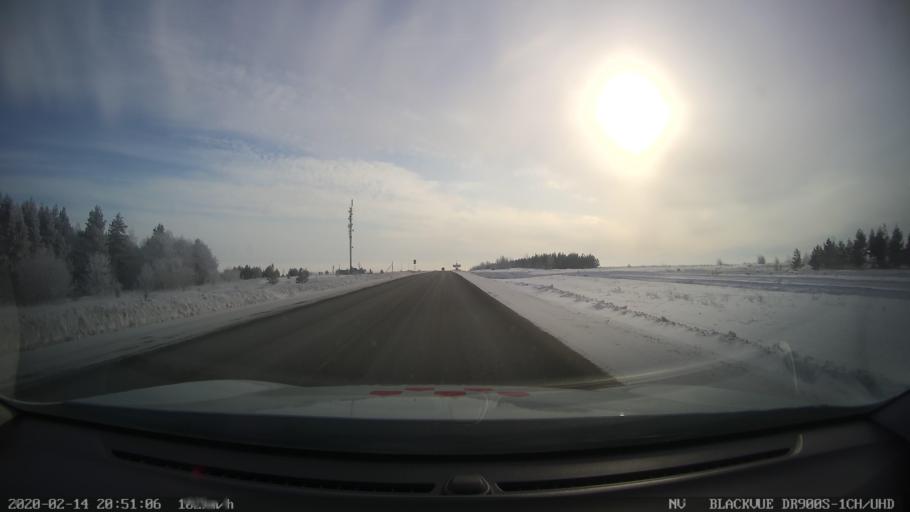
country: RU
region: Tatarstan
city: Kuybyshevskiy Zaton
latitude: 55.2169
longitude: 49.2335
